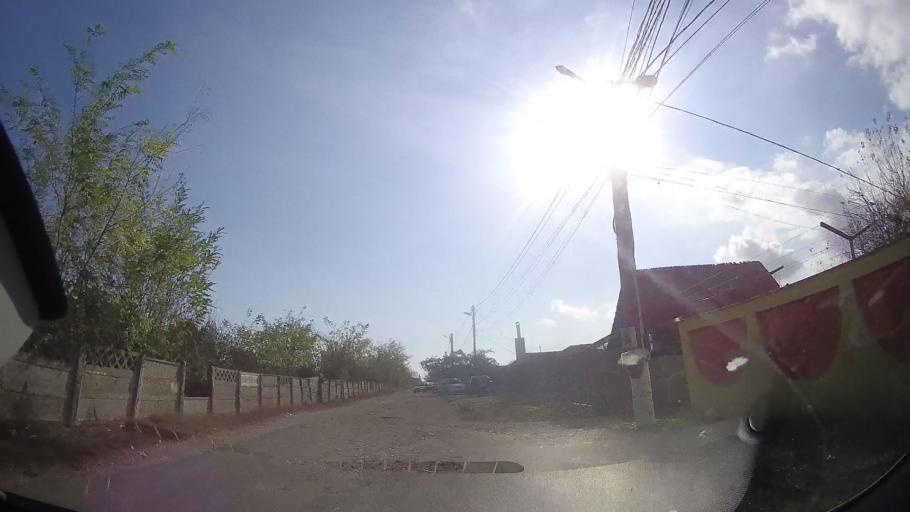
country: RO
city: Eforie Sud
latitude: 44.0132
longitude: 28.6447
